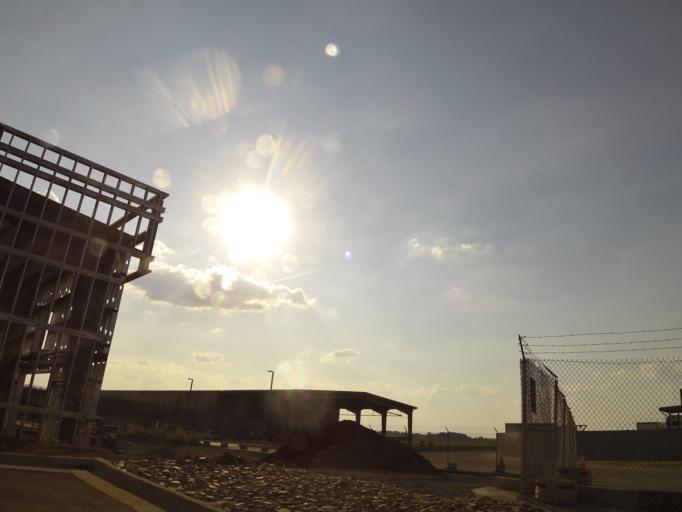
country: US
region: Tennessee
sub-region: Blount County
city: Alcoa
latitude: 35.8041
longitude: -83.9944
